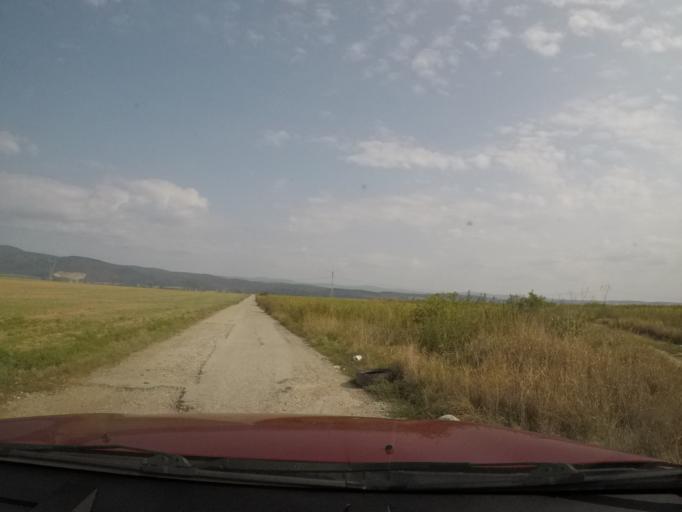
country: SK
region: Kosicky
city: Moldava nad Bodvou
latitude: 48.5826
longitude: 20.9565
